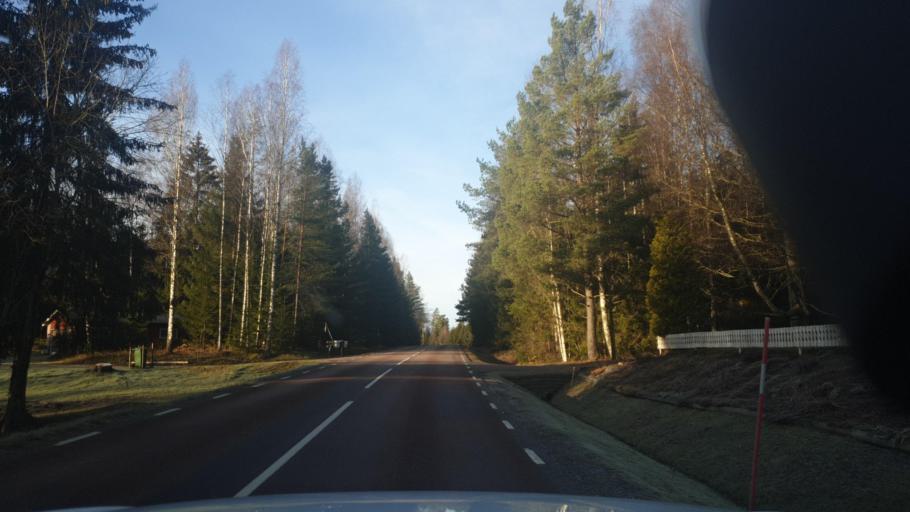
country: SE
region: Vaermland
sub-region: Grums Kommun
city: Grums
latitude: 59.4594
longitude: 12.9540
